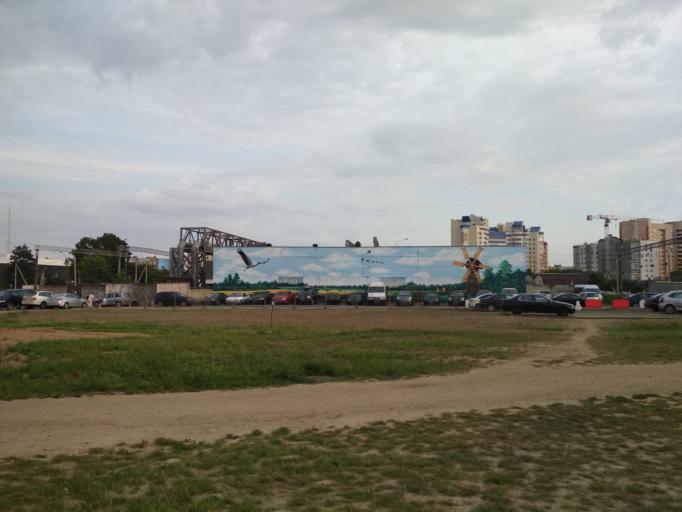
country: BY
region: Minsk
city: Minsk
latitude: 53.8888
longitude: 27.5493
